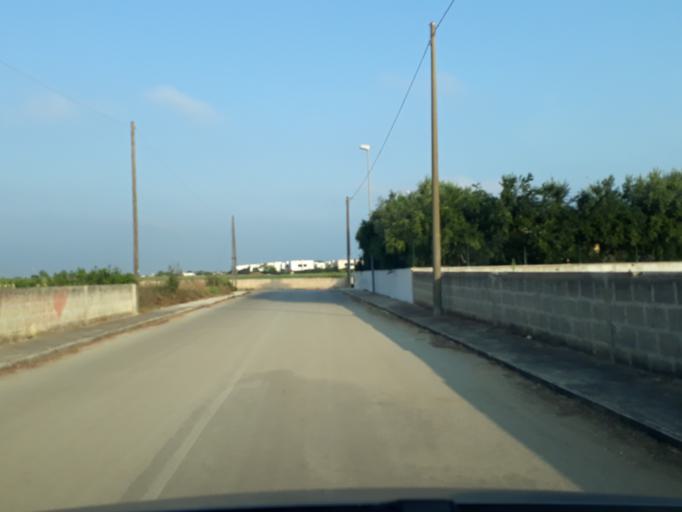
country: IT
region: Apulia
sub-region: Provincia di Brindisi
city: Carovigno
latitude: 40.7499
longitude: 17.7144
